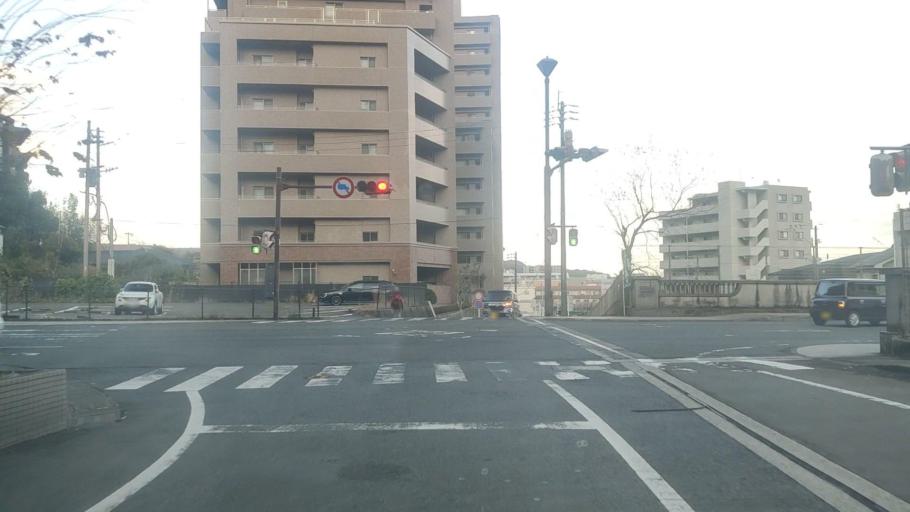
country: JP
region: Kagoshima
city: Kagoshima-shi
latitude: 31.6007
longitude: 130.5541
